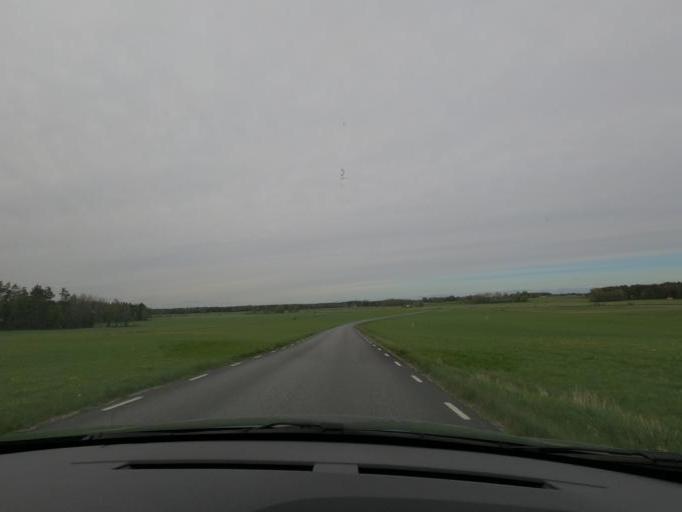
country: SE
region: Joenkoeping
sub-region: Varnamo Kommun
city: Bredaryd
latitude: 57.1266
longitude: 13.6820
